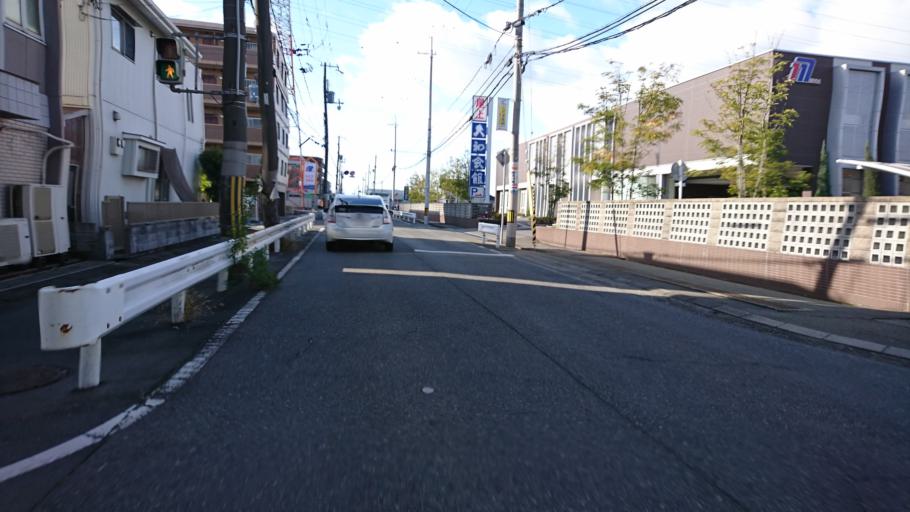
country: JP
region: Hyogo
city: Kakogawacho-honmachi
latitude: 34.7525
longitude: 134.8188
